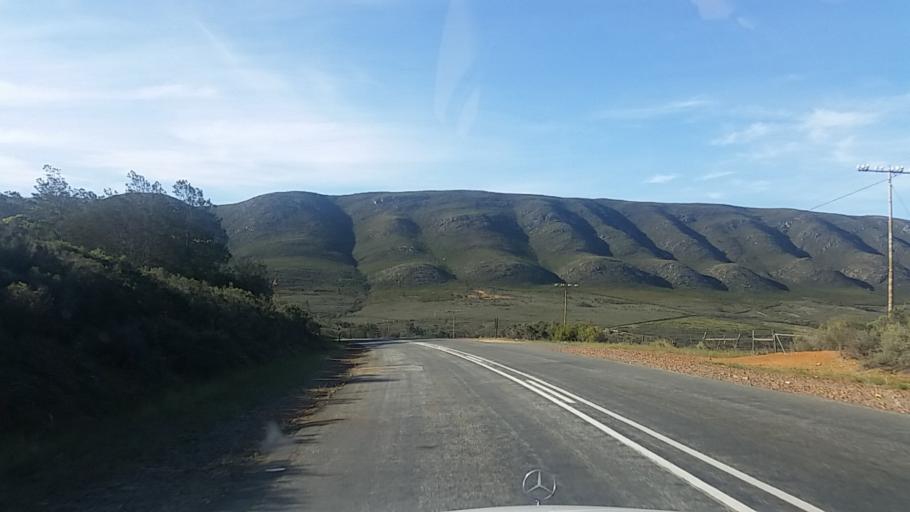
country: ZA
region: Western Cape
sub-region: Eden District Municipality
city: Knysna
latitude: -33.7700
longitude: 22.9619
